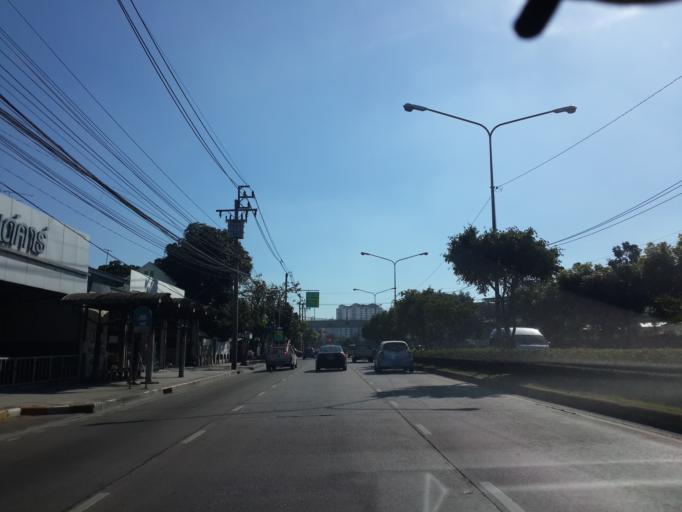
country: TH
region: Bangkok
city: Bang Kapi
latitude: 13.7820
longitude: 100.6462
